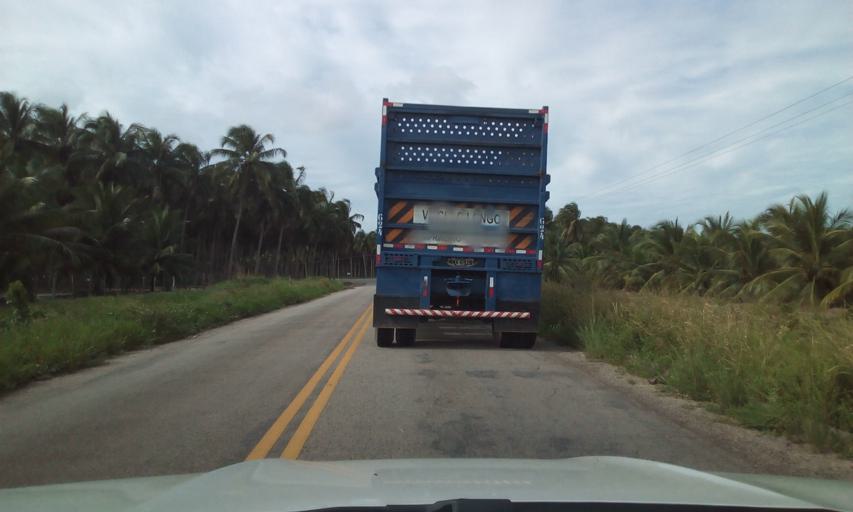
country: BR
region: Paraiba
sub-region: Cabedelo
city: Cabedelo
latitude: -6.9391
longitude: -34.9057
